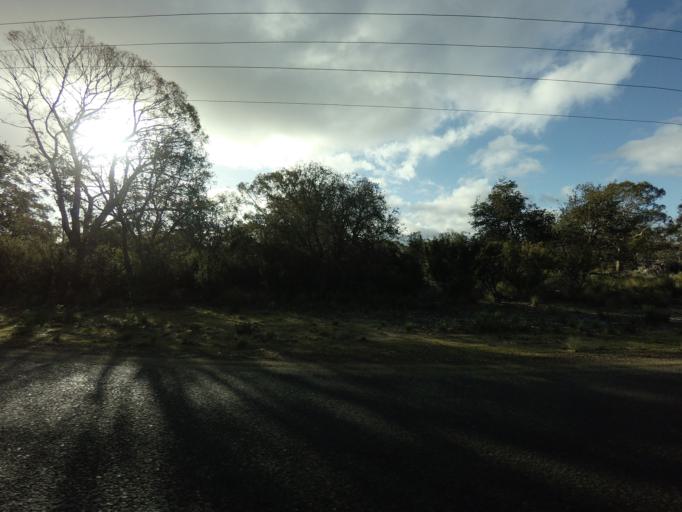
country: AU
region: Tasmania
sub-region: Break O'Day
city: St Helens
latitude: -42.0913
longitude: 148.1112
